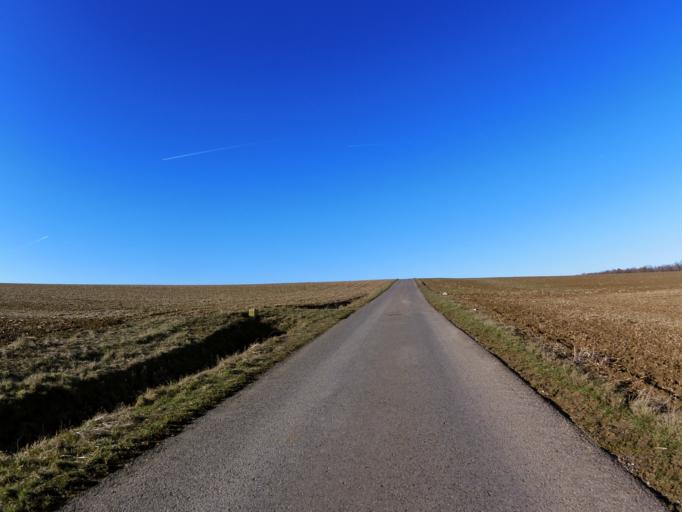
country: DE
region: Bavaria
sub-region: Regierungsbezirk Unterfranken
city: Estenfeld
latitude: 49.8464
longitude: 9.9985
